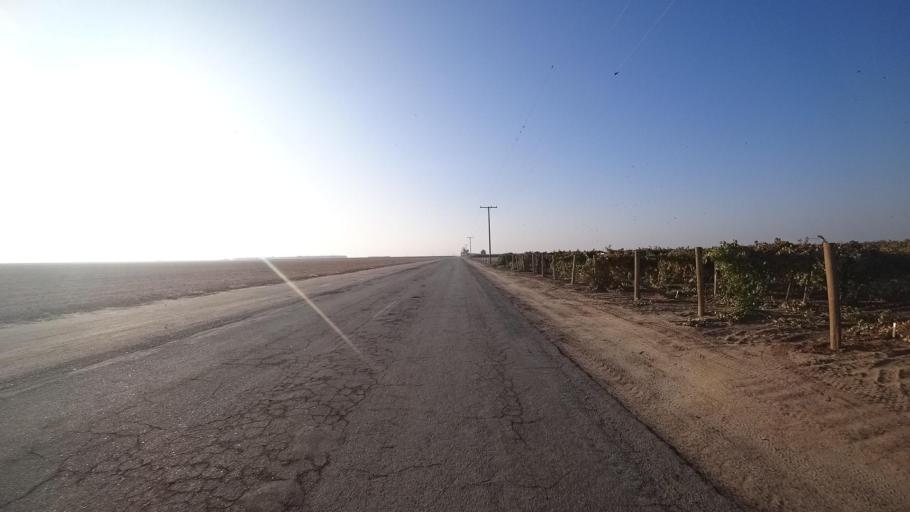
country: US
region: California
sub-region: Tulare County
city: Richgrove
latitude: 35.7859
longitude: -119.1341
